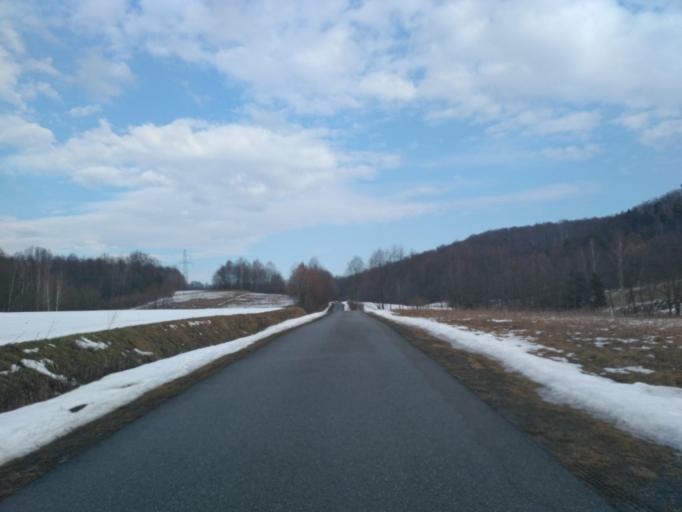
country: PL
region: Subcarpathian Voivodeship
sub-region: Powiat brzozowski
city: Niebocko
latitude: 49.6441
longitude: 22.1300
